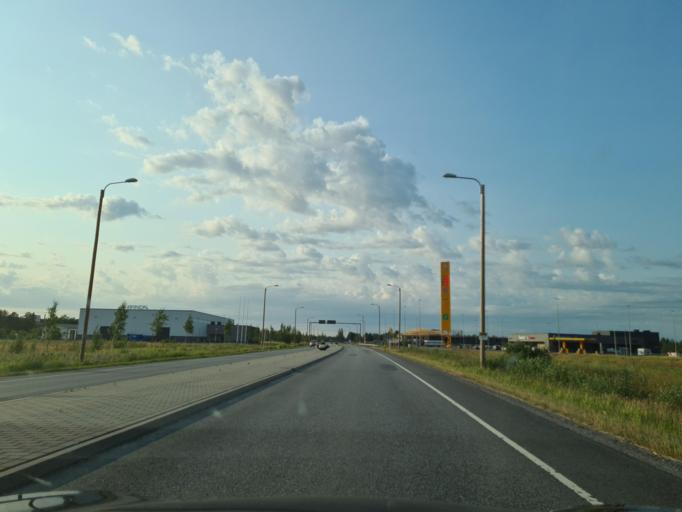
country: FI
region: Southern Ostrobothnia
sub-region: Seinaejoki
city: Kauhava
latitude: 63.0884
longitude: 23.0589
